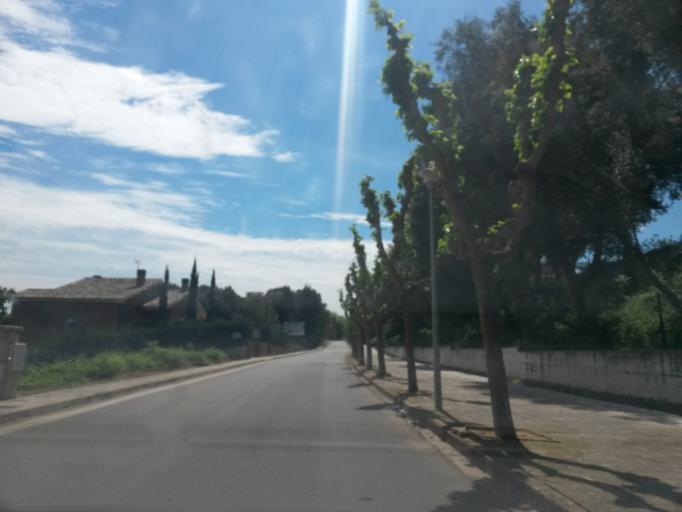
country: ES
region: Catalonia
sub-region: Provincia de Girona
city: Vilablareix
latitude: 41.9652
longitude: 2.7627
